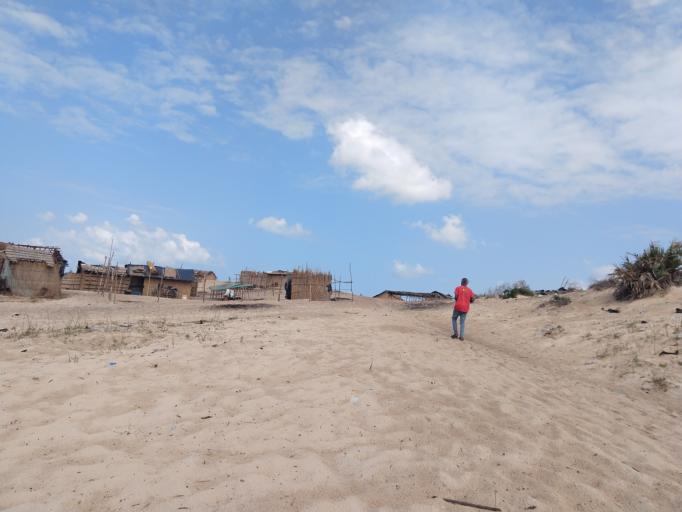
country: MZ
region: Sofala
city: Beira
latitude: -19.6475
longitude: 35.1794
